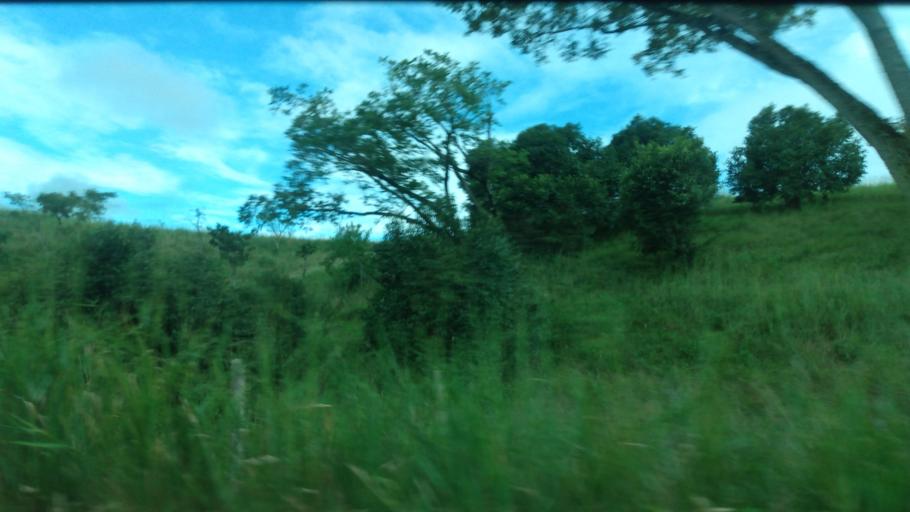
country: BR
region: Pernambuco
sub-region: Catende
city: Catende
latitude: -8.6943
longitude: -35.7279
